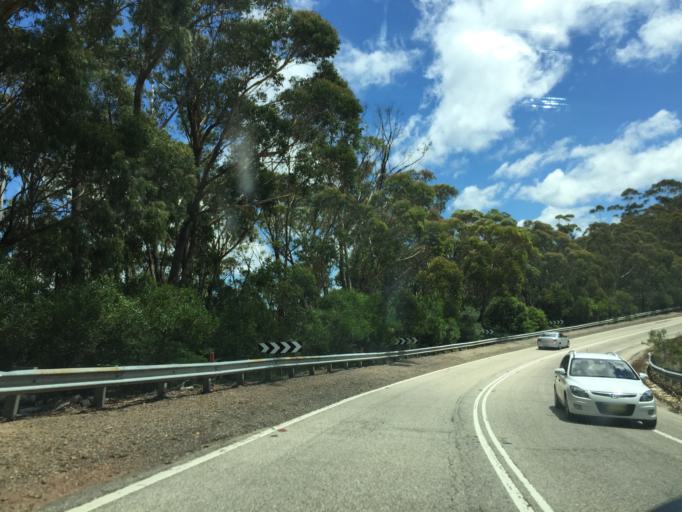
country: AU
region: New South Wales
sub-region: Blue Mountains Municipality
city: Blackheath
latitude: -33.5502
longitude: 150.3994
